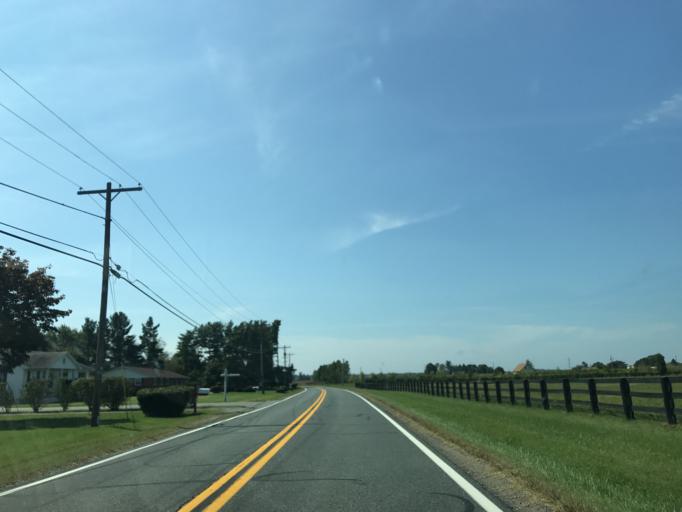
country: US
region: Maryland
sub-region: Cecil County
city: Elkton
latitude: 39.4897
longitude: -75.8375
